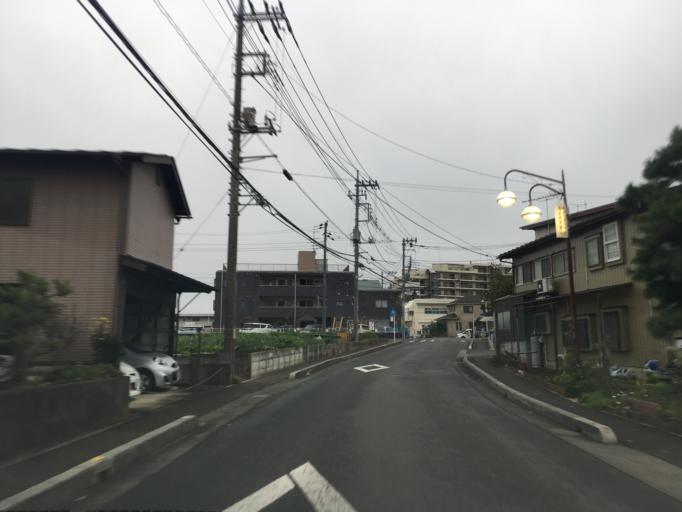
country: JP
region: Saitama
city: Tokorozawa
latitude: 35.7887
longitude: 139.4312
